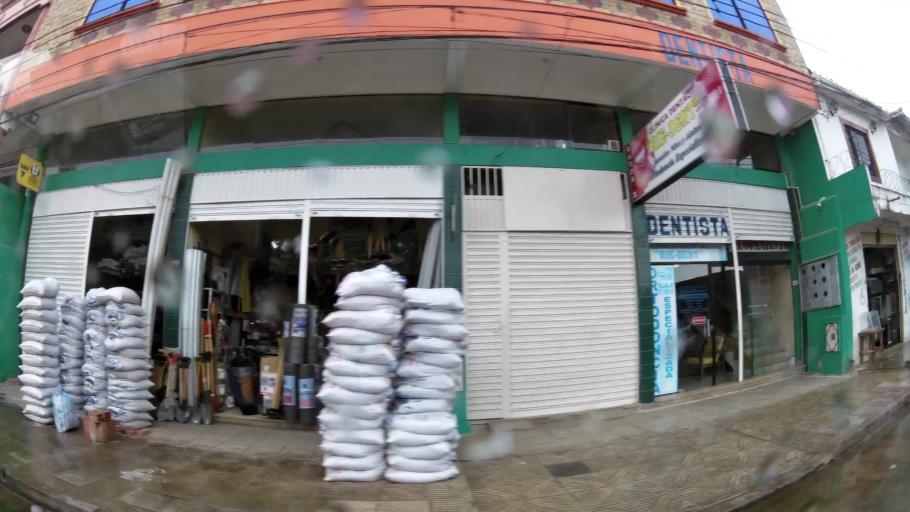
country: BO
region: Santa Cruz
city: Santa Cruz de la Sierra
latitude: -17.8119
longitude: -63.1906
